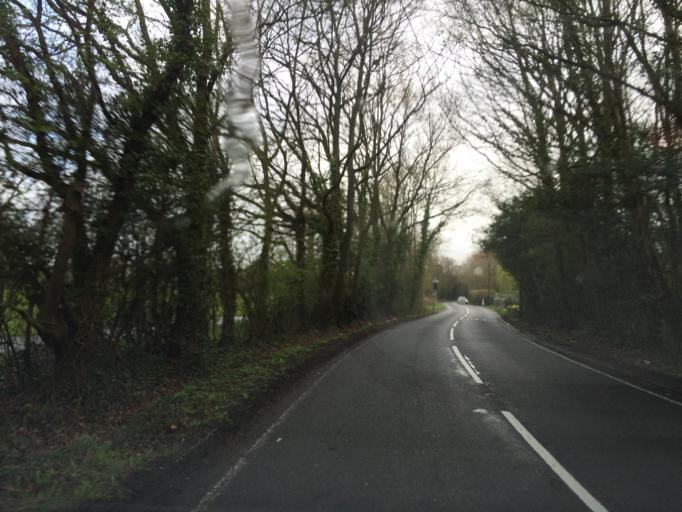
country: GB
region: England
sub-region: Surrey
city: Knaphill
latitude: 51.3314
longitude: -0.6127
